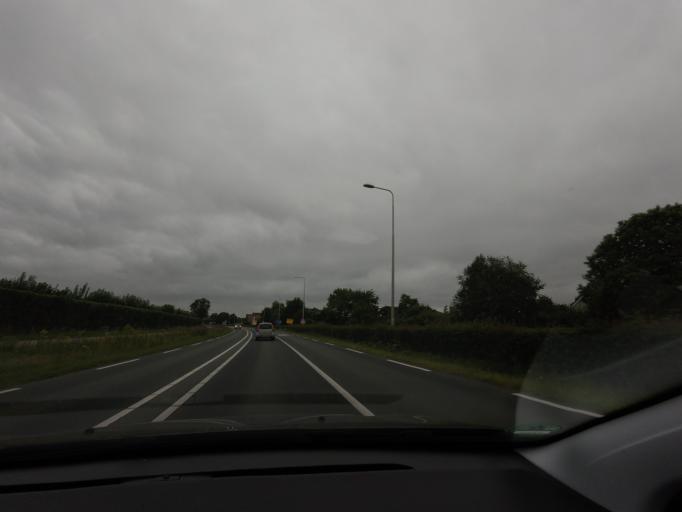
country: NL
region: Utrecht
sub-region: Gemeente Bunnik
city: Bunnik
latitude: 52.0512
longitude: 5.2281
